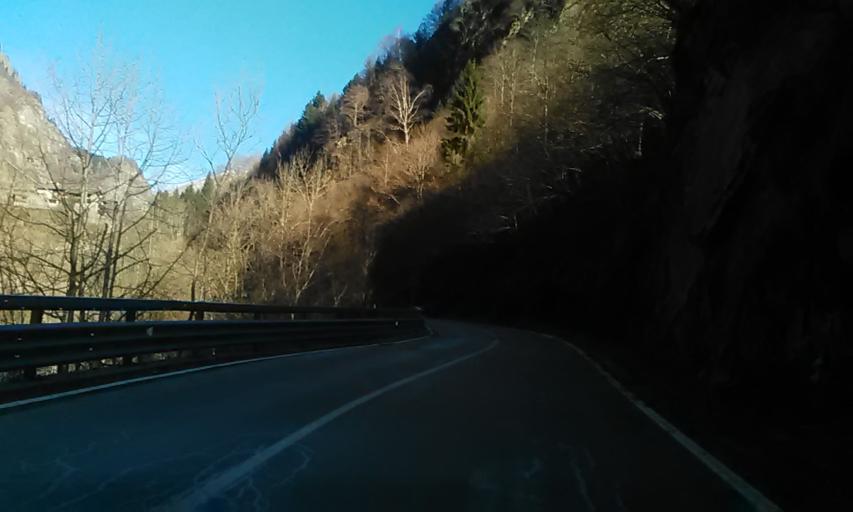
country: IT
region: Piedmont
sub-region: Provincia di Vercelli
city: Rimasco
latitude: 45.8524
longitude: 8.0645
